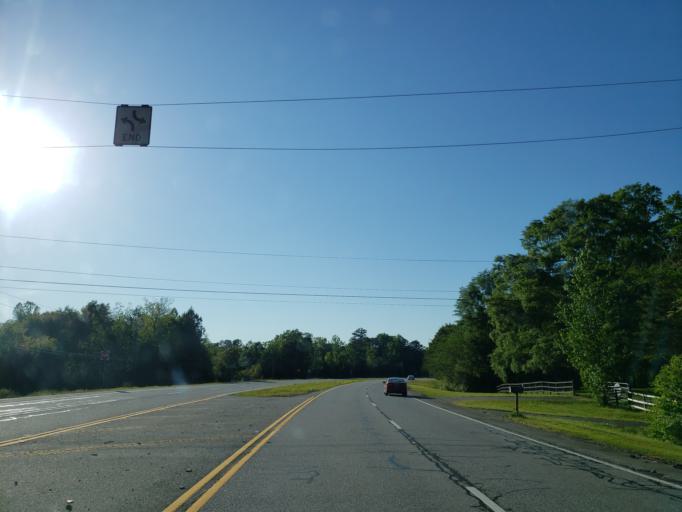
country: US
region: Georgia
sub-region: Haralson County
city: Buchanan
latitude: 33.8977
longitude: -85.2311
